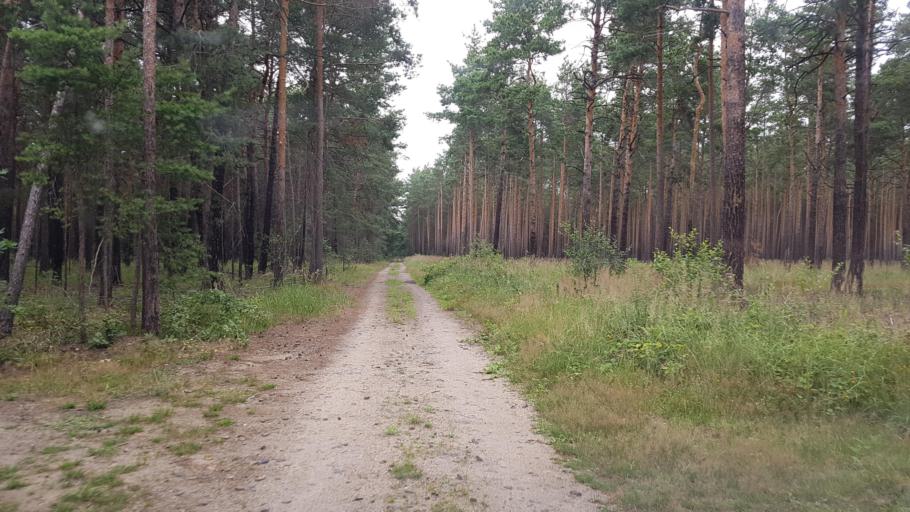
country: DE
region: Brandenburg
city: Grossraschen
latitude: 51.5937
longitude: 14.0369
